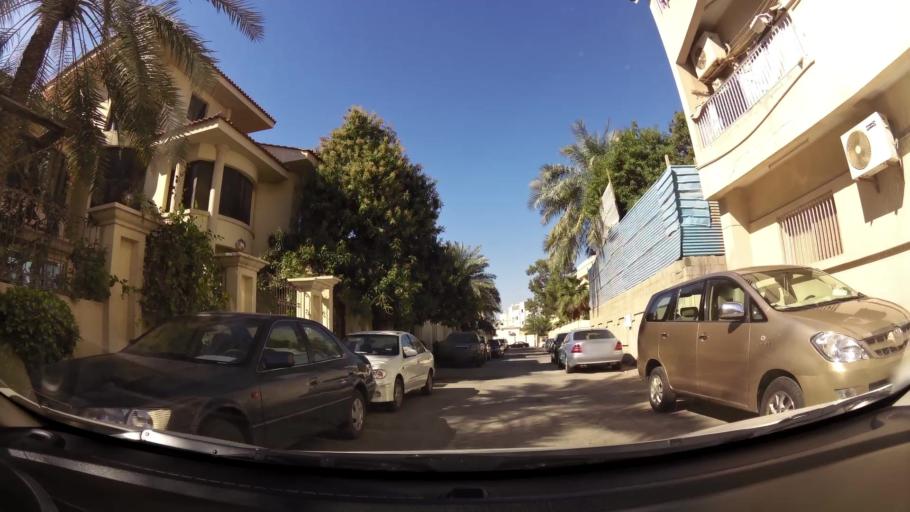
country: BH
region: Muharraq
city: Al Muharraq
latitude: 26.2635
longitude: 50.6205
